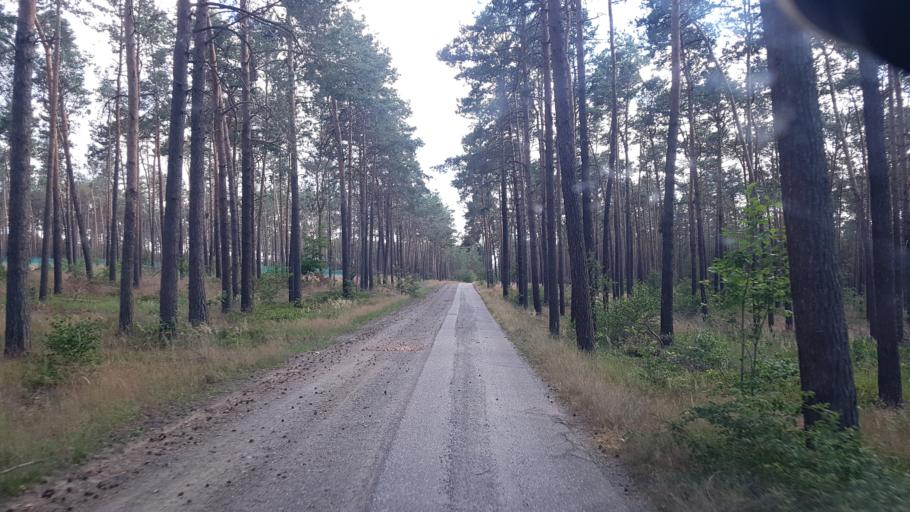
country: DE
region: Brandenburg
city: Trobitz
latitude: 51.6222
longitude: 13.4296
